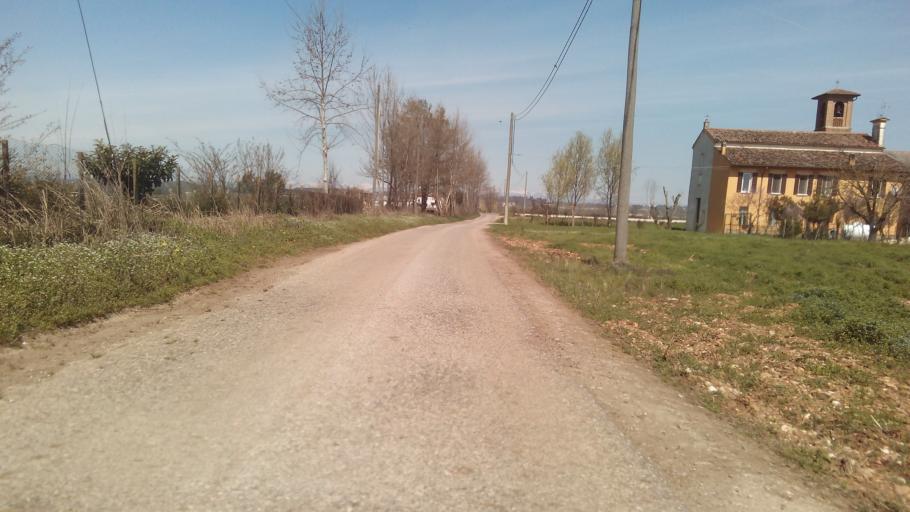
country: IT
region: Lombardy
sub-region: Provincia di Mantova
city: Cerlongo
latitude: 45.2840
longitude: 10.6684
